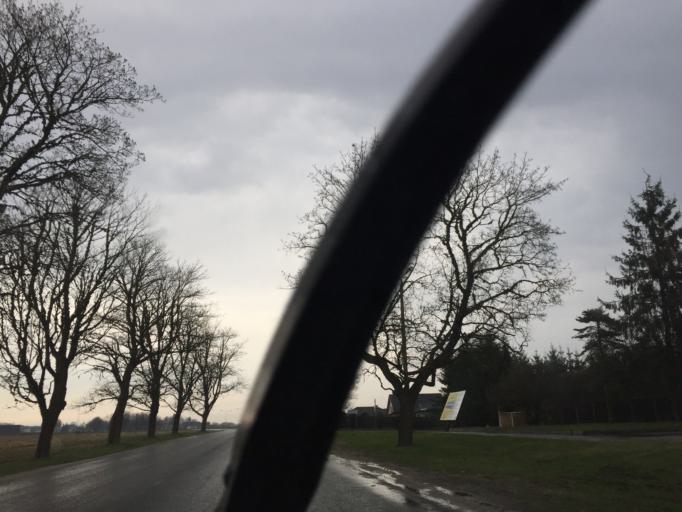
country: EE
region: Tartu
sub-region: UElenurme vald
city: Ulenurme
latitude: 58.3233
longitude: 26.7214
